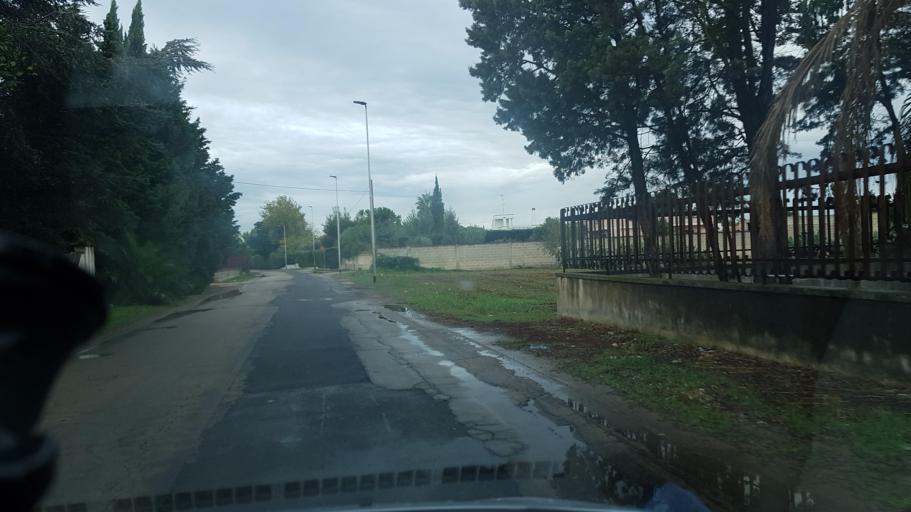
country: IT
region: Apulia
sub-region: Provincia di Lecce
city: Carmiano
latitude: 40.3519
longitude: 18.0354
